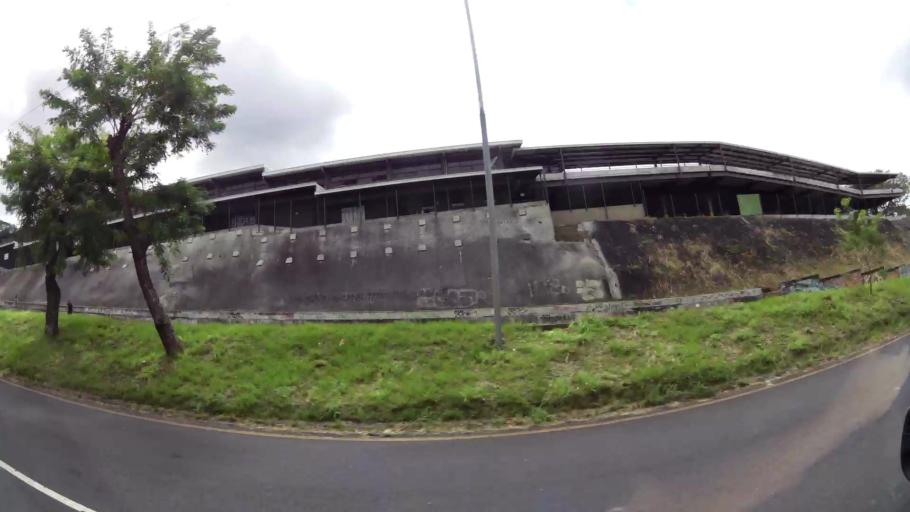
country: CR
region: San Jose
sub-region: Canton de Goicoechea
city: Guadalupe
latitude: 9.9409
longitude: -84.0557
